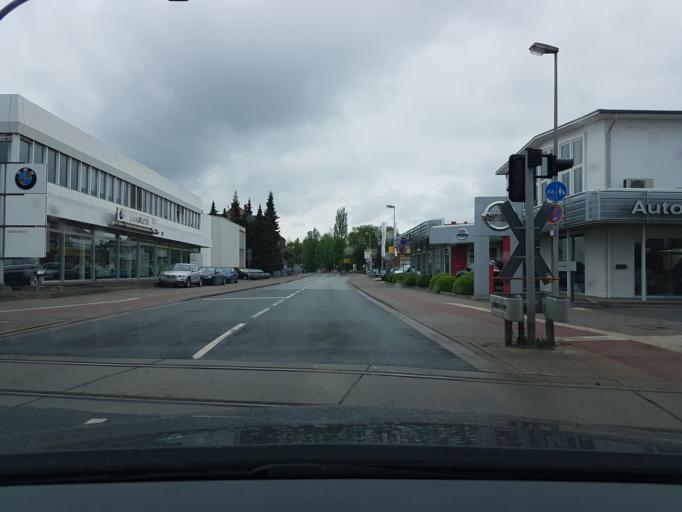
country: DE
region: Lower Saxony
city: Hameln
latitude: 52.0956
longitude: 9.3695
